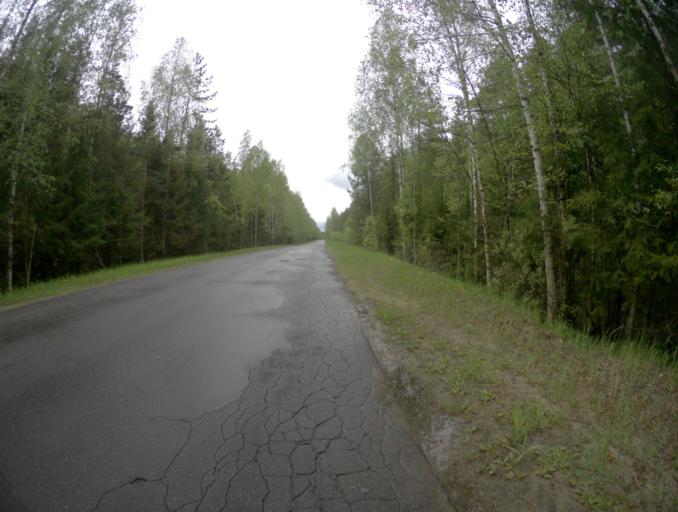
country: RU
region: Vladimir
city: Zolotkovo
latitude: 55.3463
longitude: 40.9744
